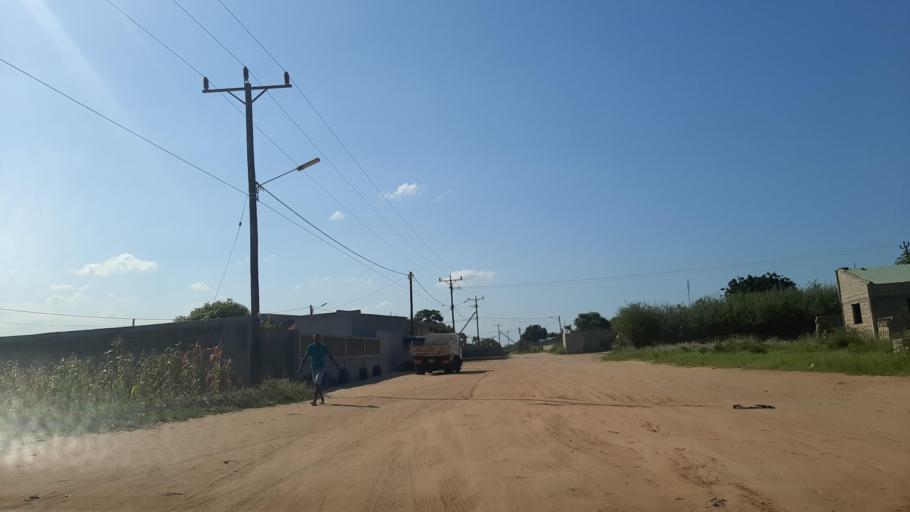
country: MZ
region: Maputo
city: Matola
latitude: -25.7960
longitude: 32.4897
